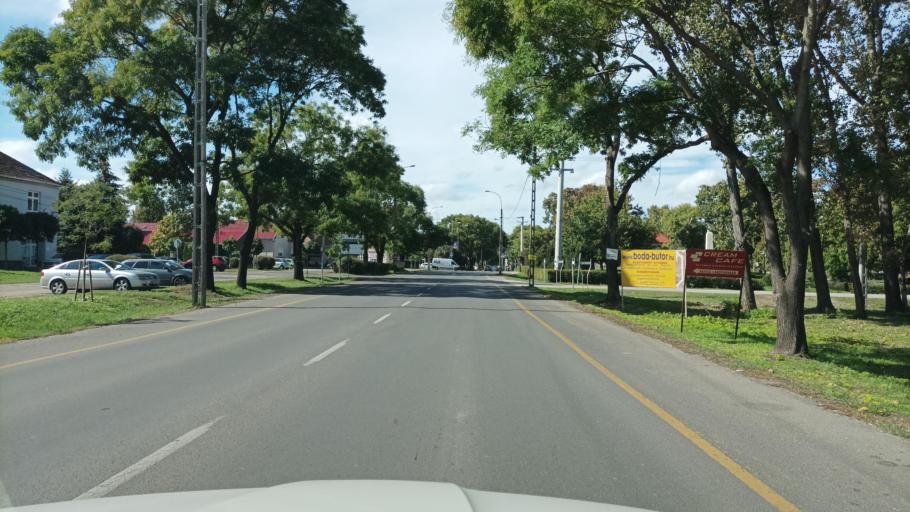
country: HU
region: Pest
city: Vecses
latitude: 47.4065
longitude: 19.2829
